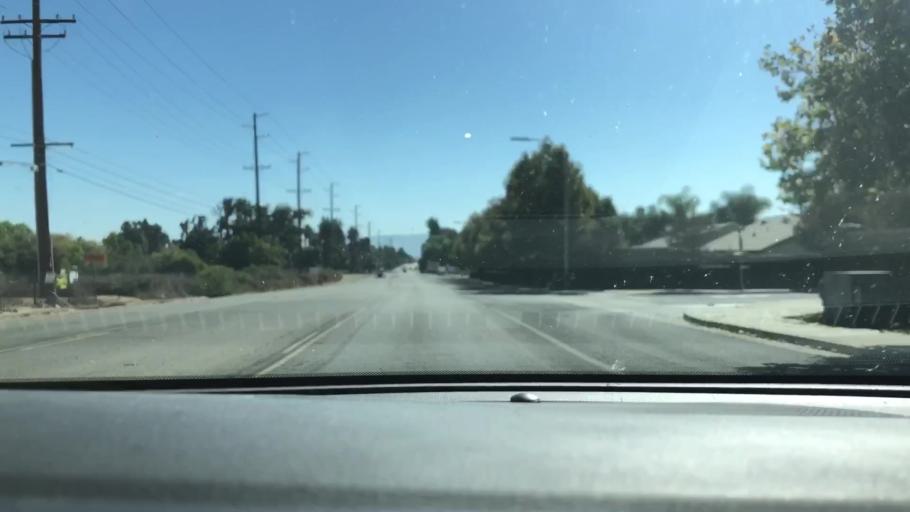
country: US
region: California
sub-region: Riverside County
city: Wildomar
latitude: 33.5999
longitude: -117.2672
